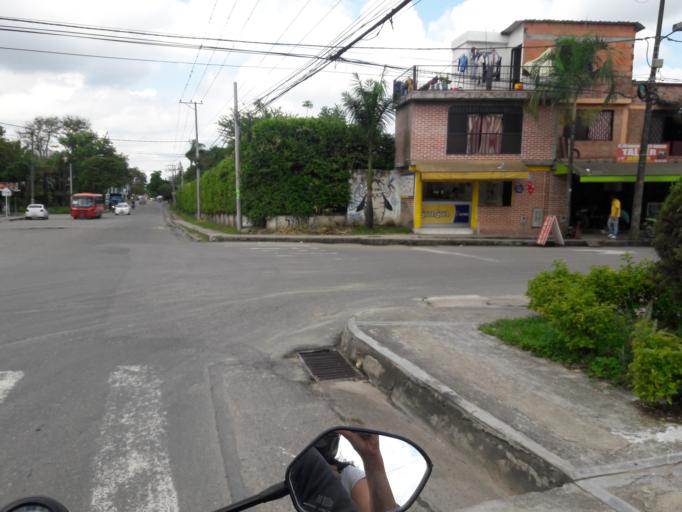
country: CO
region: Tolima
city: Ibague
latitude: 4.4471
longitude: -75.1598
